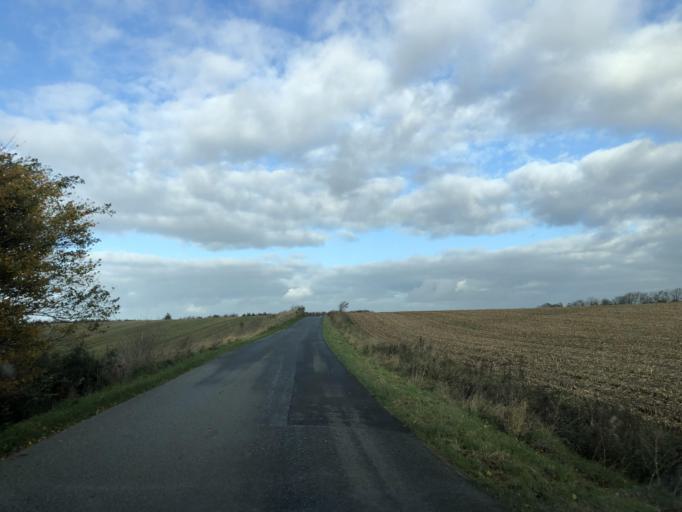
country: DK
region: Central Jutland
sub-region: Holstebro Kommune
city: Ulfborg
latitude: 56.1906
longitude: 8.4215
